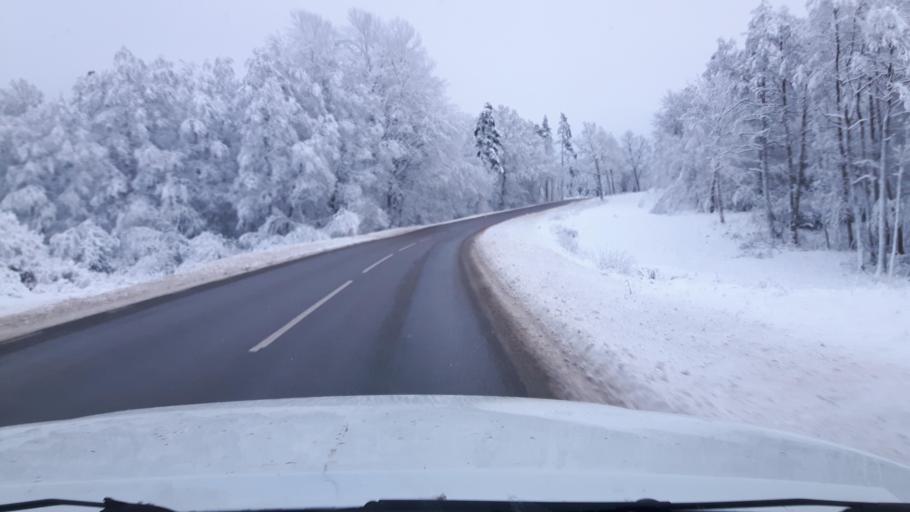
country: SE
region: Halland
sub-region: Kungsbacka Kommun
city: Fjaeras kyrkby
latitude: 57.4171
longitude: 12.2097
